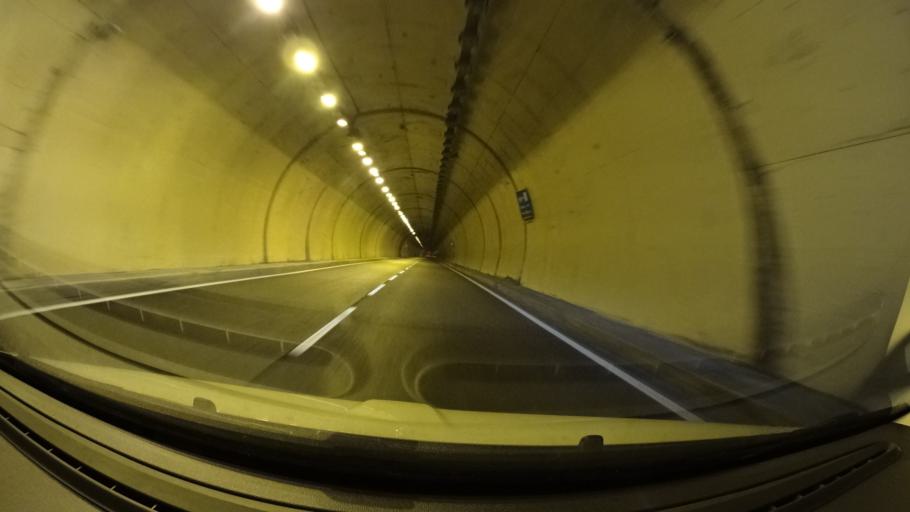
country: IT
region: Trentino-Alto Adige
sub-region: Provincia di Trento
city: Mori
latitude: 45.8435
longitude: 10.9872
